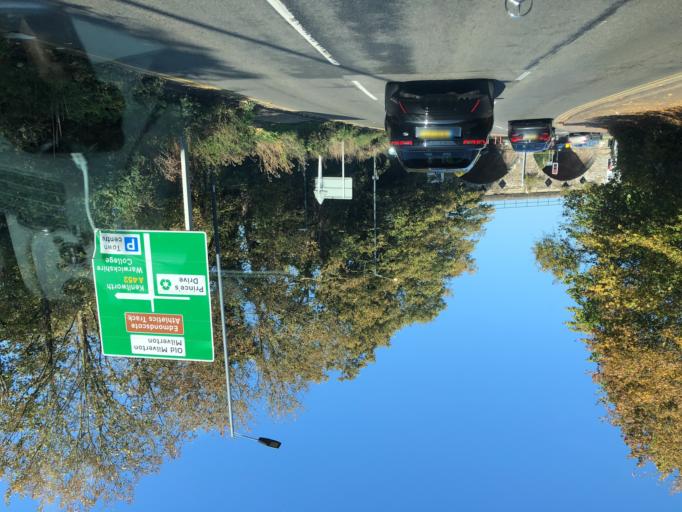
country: GB
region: England
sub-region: Warwickshire
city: Royal Leamington Spa
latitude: 52.2854
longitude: -1.5471
